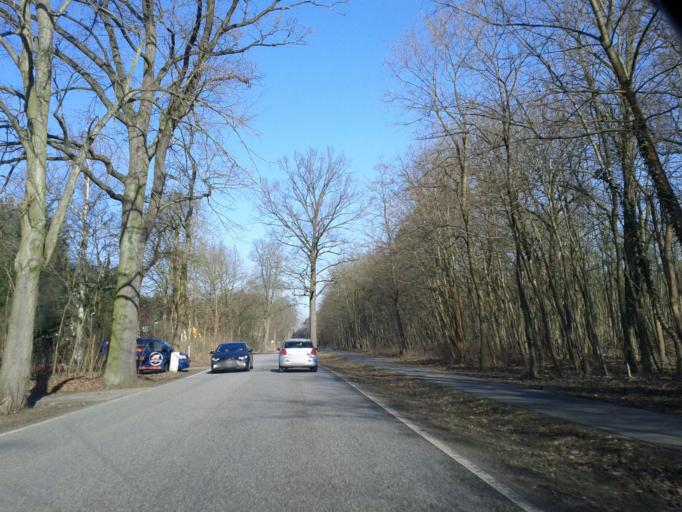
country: DE
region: Brandenburg
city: Woltersdorf
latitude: 52.4393
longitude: 13.7556
